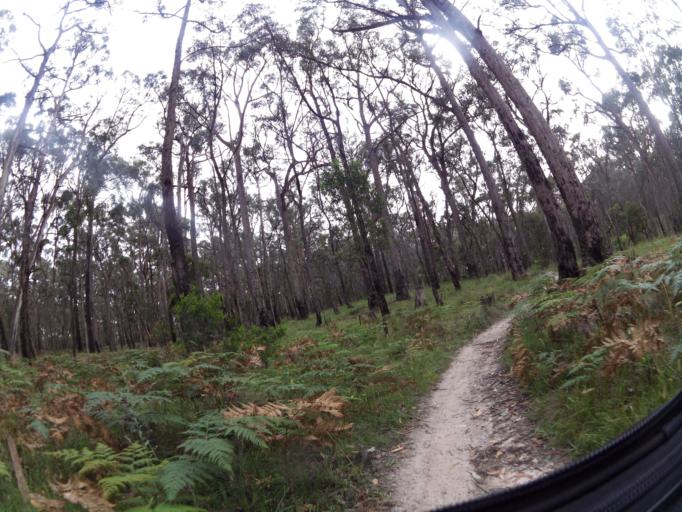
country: AU
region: Victoria
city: Brown Hill
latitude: -37.5253
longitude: 143.9055
